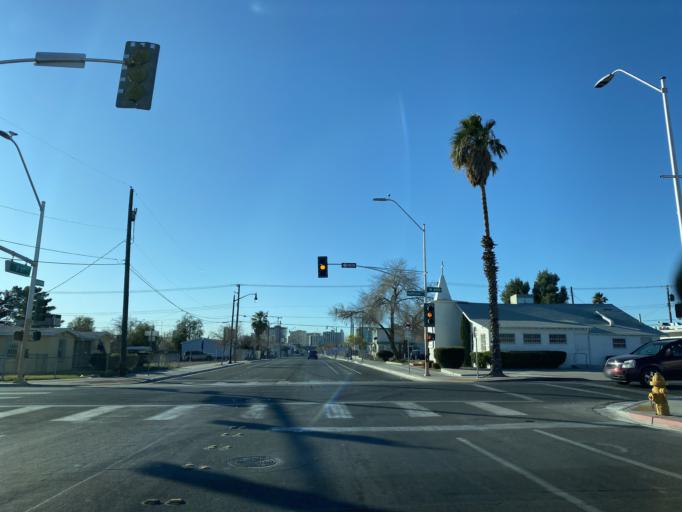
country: US
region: Nevada
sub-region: Clark County
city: Las Vegas
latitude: 36.1882
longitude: -115.1472
